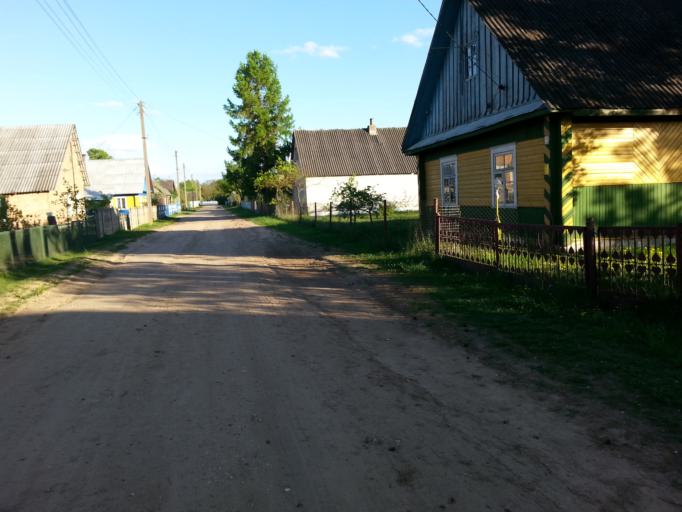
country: BY
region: Minsk
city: Narach
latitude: 54.9324
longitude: 26.6827
